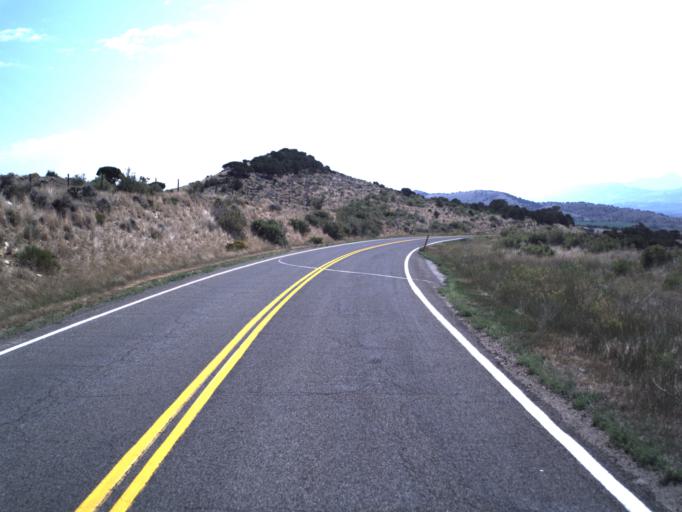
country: US
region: Utah
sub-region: Daggett County
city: Manila
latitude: 40.9789
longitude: -109.7884
